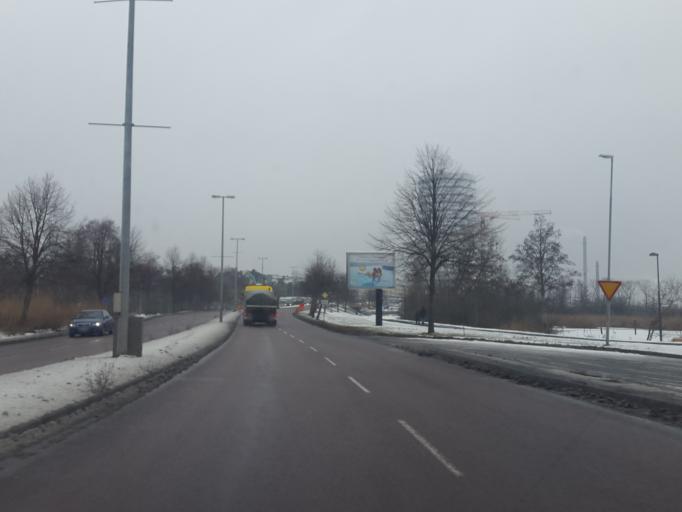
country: SE
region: Joenkoeping
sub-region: Jonkopings Kommun
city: Jonkoping
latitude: 57.7656
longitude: 14.1536
